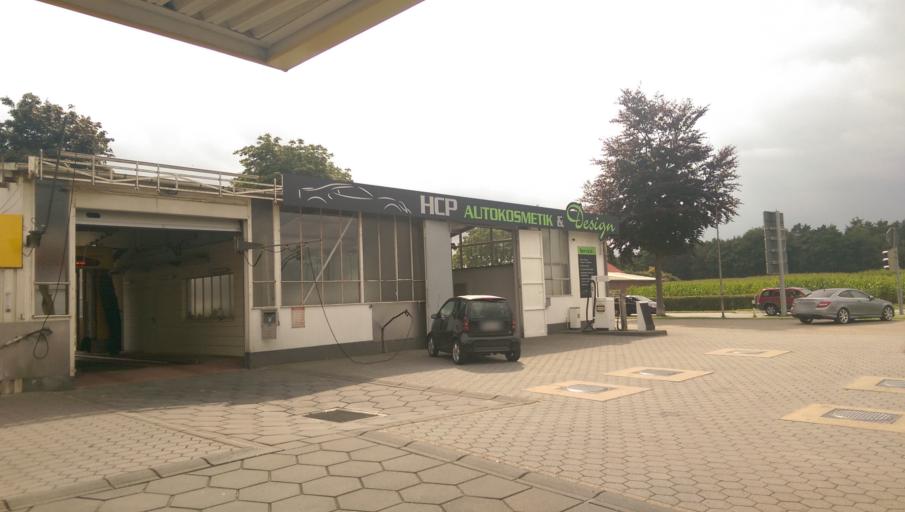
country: DE
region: Lower Saxony
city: Bockhorn
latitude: 53.3849
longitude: 8.0576
